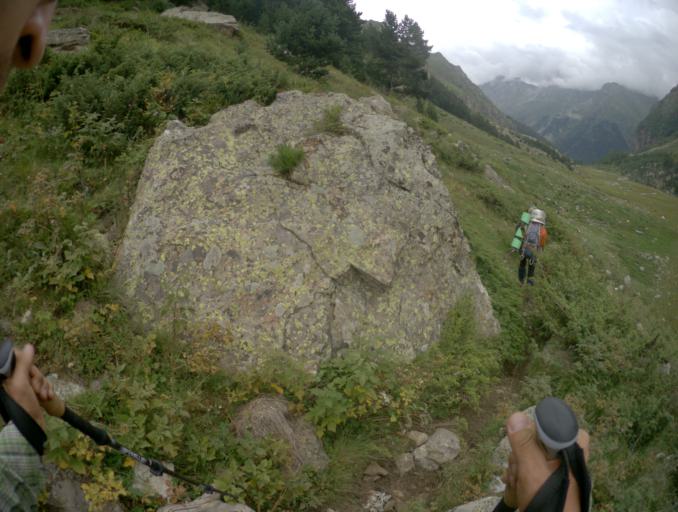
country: RU
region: Karachayevo-Cherkesiya
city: Uchkulan
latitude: 43.2669
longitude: 42.1396
